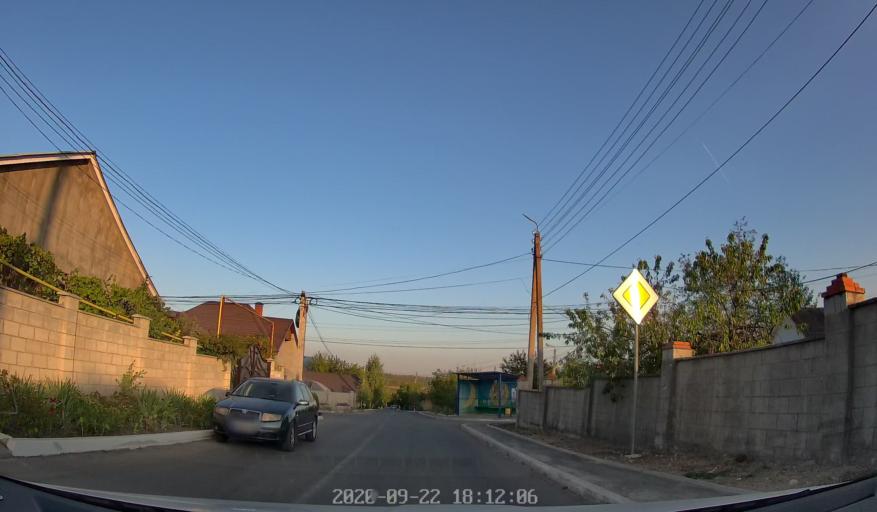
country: MD
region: Laloveni
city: Ialoveni
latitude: 46.9483
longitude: 28.7867
